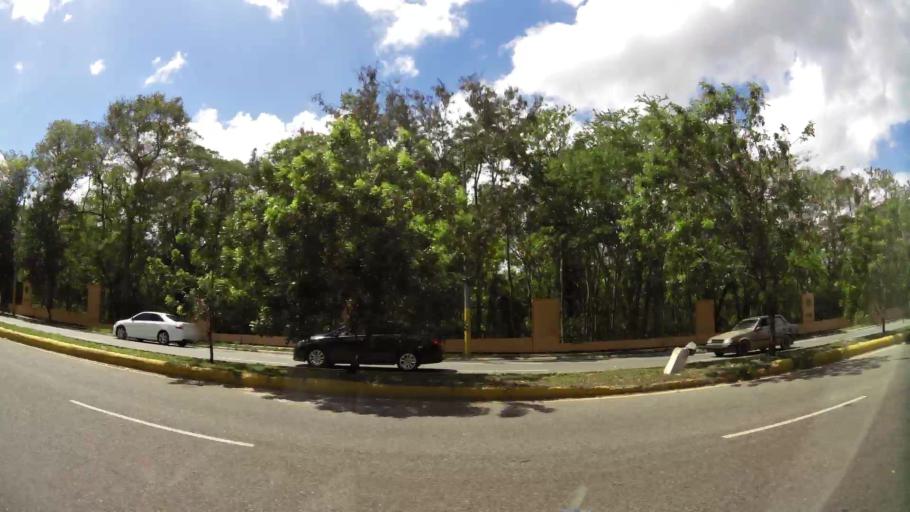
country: DO
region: Nacional
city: La Agustina
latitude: 18.5187
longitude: -69.9215
